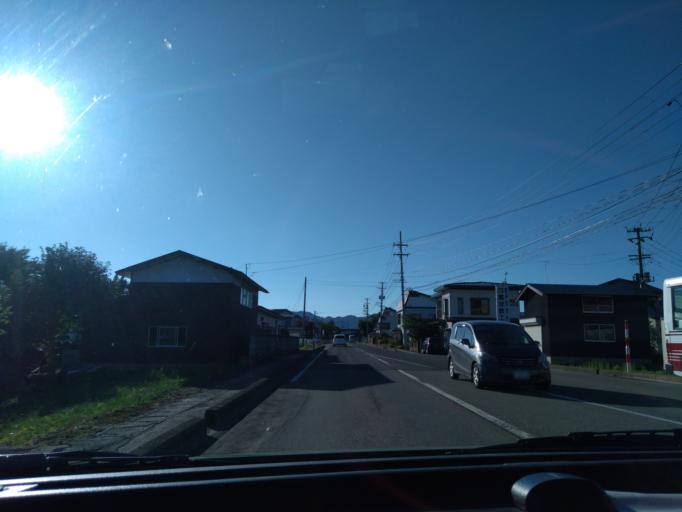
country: JP
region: Akita
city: Omagari
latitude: 39.4276
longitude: 140.4896
